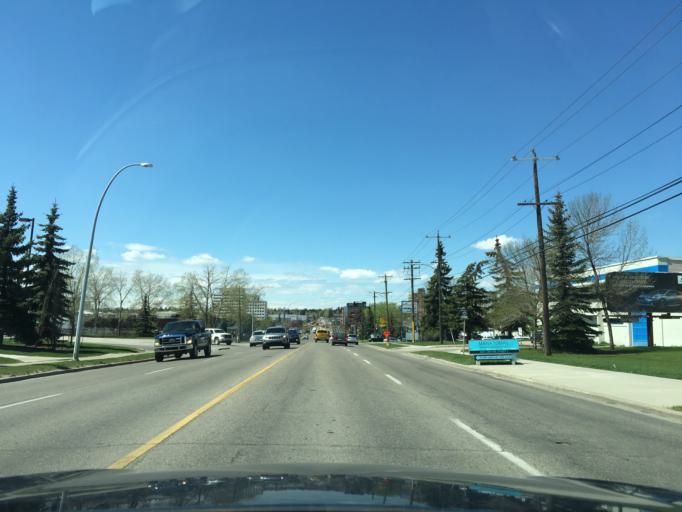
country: CA
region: Alberta
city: Calgary
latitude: 51.0014
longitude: -114.0603
